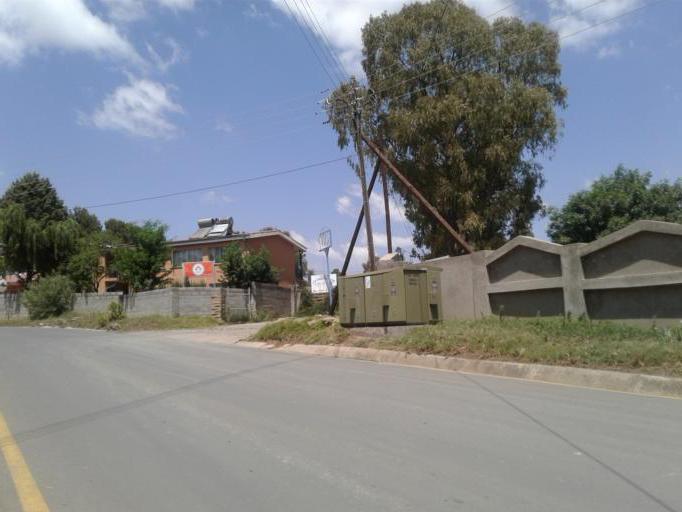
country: LS
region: Maseru
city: Maseru
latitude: -29.3086
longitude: 27.4821
